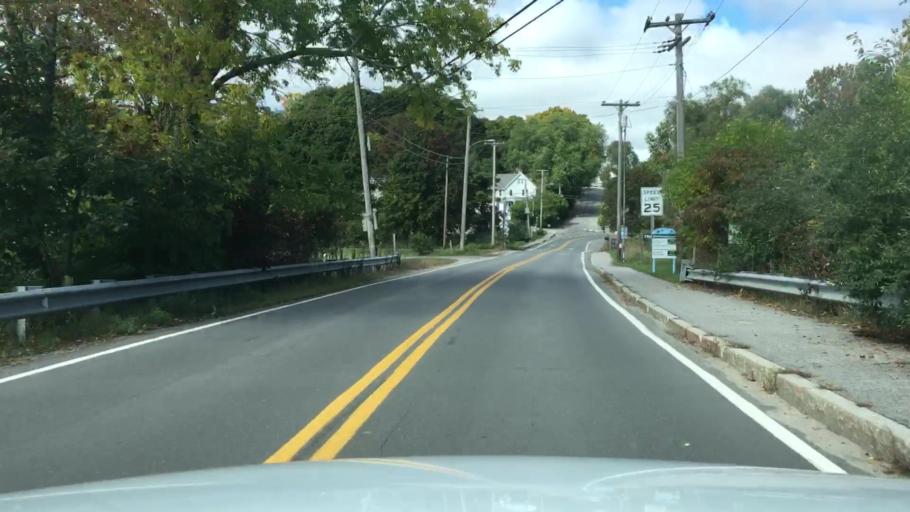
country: US
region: Maine
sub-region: Sagadahoc County
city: North Bath
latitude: 44.0073
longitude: -69.8957
